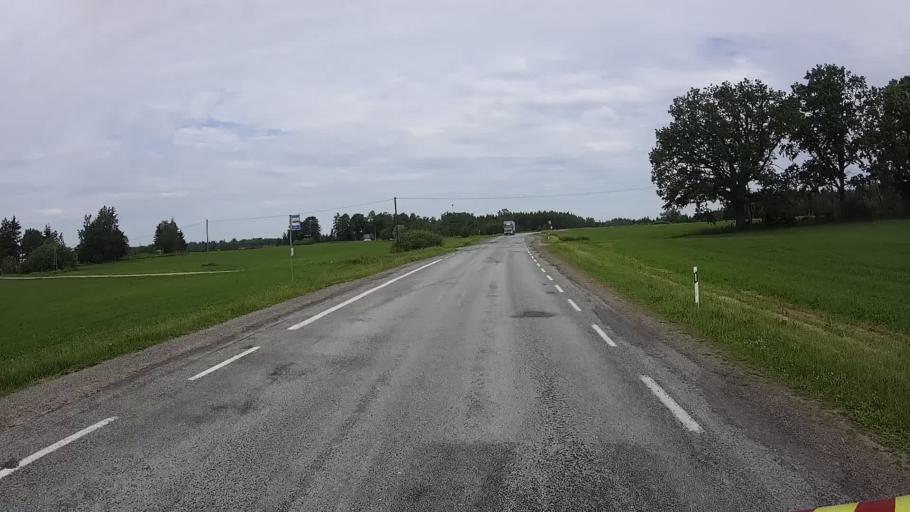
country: EE
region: Viljandimaa
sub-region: Karksi vald
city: Karksi-Nuia
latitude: 58.2292
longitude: 25.6044
